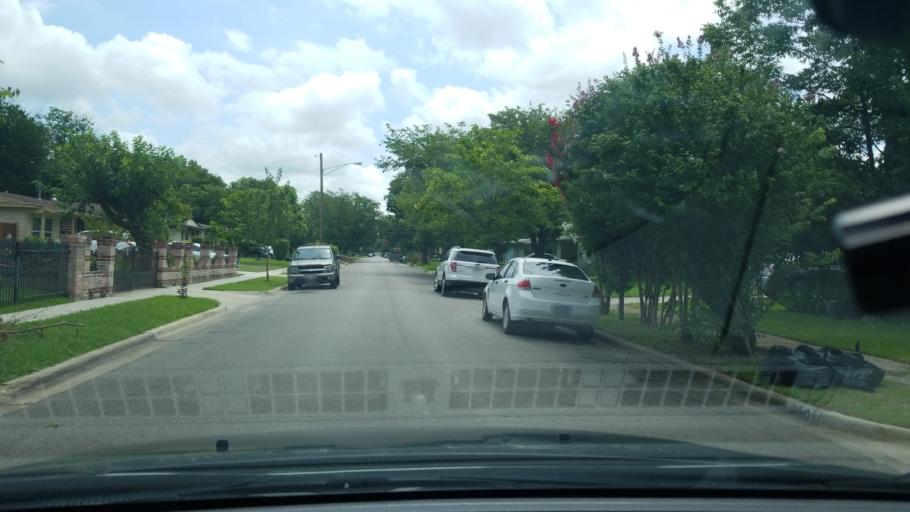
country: US
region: Texas
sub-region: Dallas County
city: Mesquite
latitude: 32.8133
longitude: -96.6752
